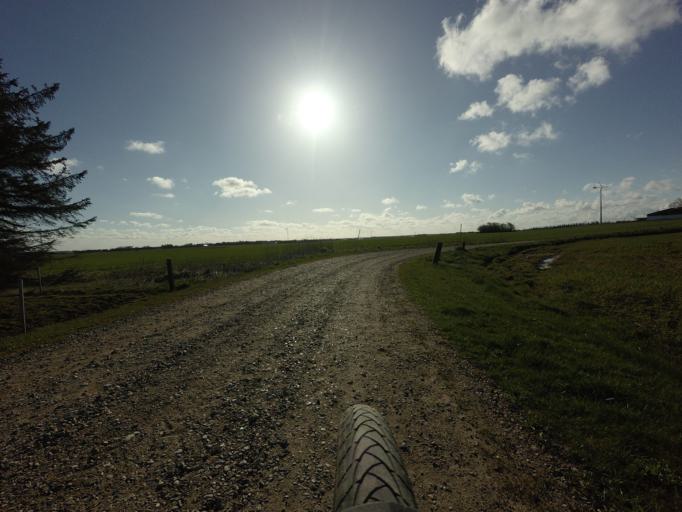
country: DK
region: North Denmark
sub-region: Hjorring Kommune
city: Vra
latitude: 57.3664
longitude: 9.8167
